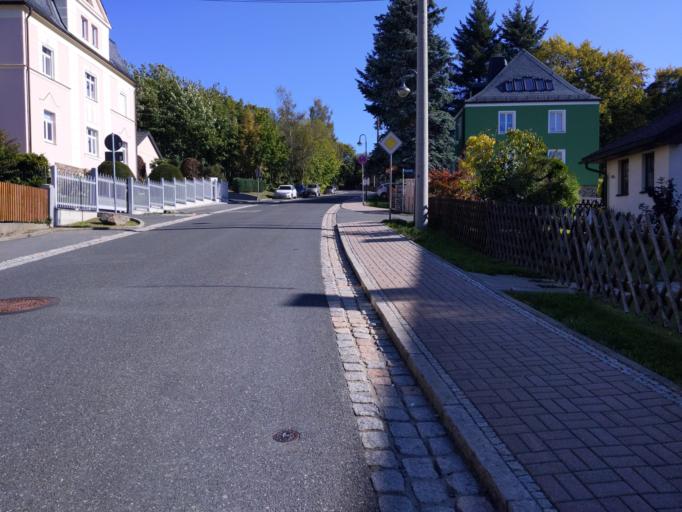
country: DE
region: Saxony
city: Pohl
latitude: 50.3935
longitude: 12.3361
